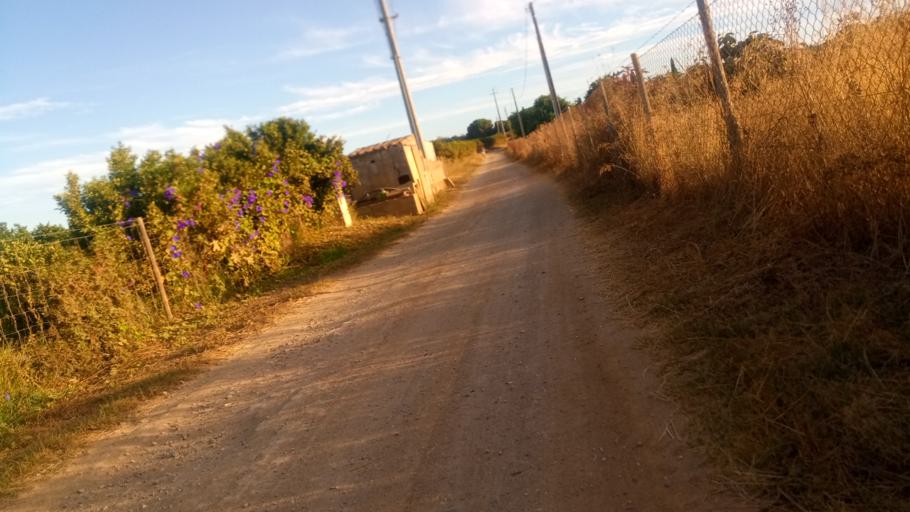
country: PT
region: Faro
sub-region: Tavira
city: Tavira
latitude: 37.1495
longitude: -7.5868
